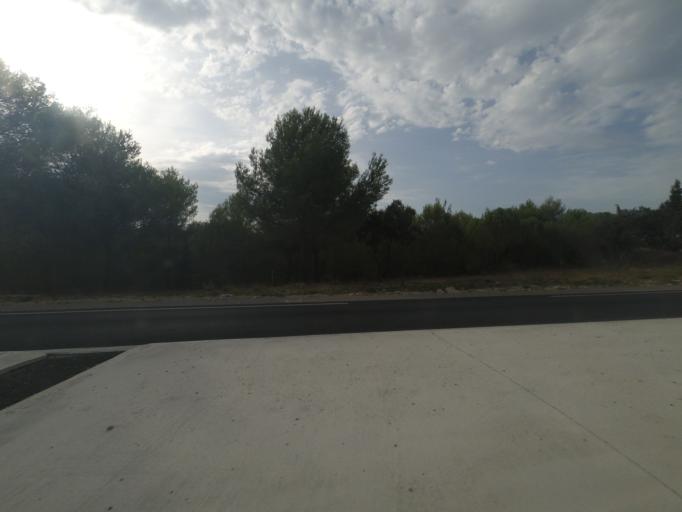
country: FR
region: Languedoc-Roussillon
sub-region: Departement de l'Herault
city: Saint-Genies-des-Mourgues
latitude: 43.7043
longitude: 4.0247
